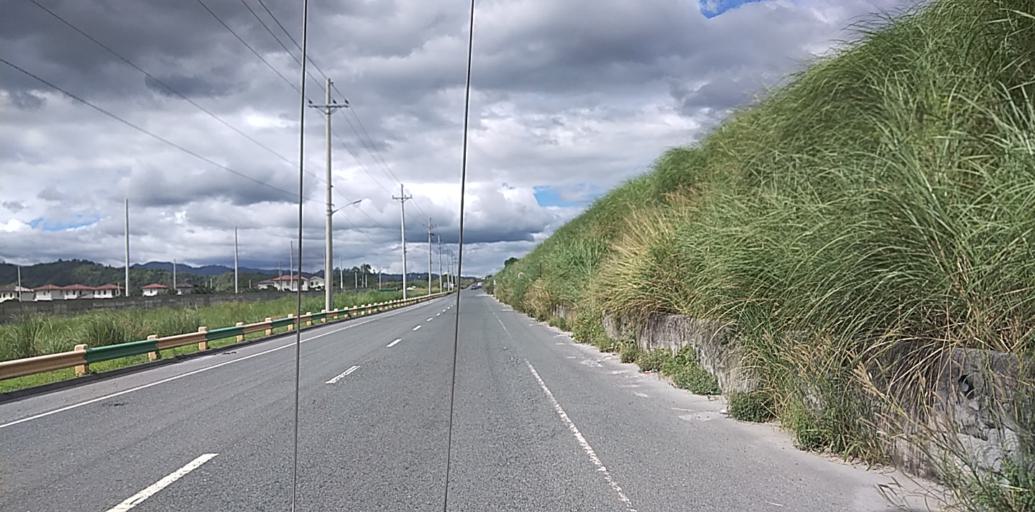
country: PH
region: Central Luzon
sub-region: Province of Pampanga
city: Dolores
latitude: 15.1138
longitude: 120.5162
